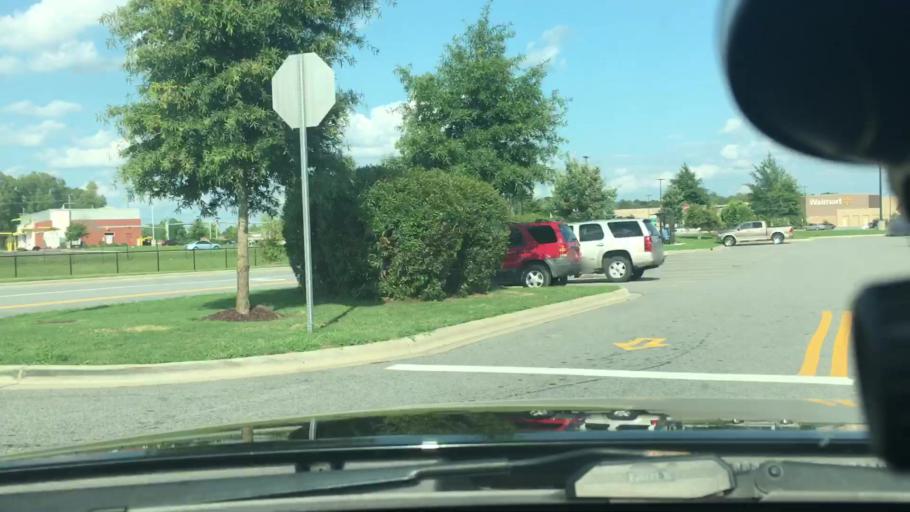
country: US
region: North Carolina
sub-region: Pitt County
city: Windsor
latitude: 35.5809
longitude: -77.3098
